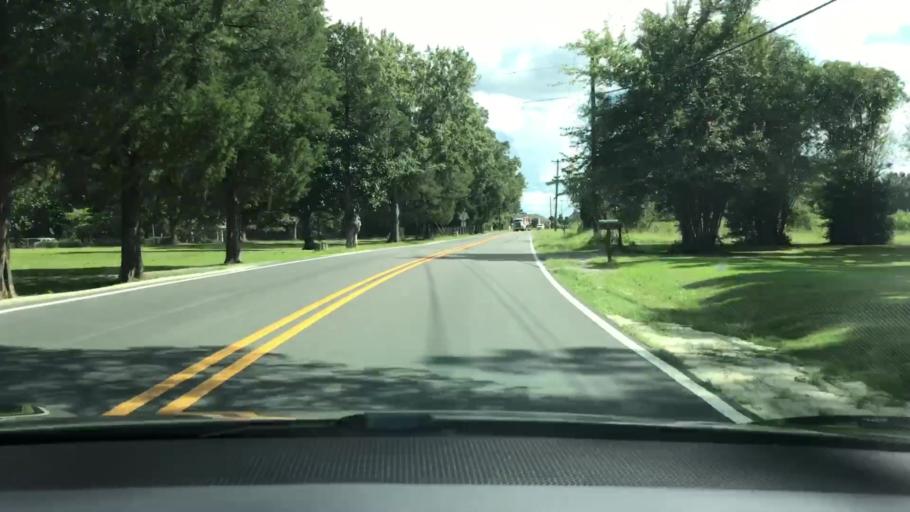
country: US
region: Alabama
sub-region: Montgomery County
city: Pike Road
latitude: 32.3585
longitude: -86.0952
